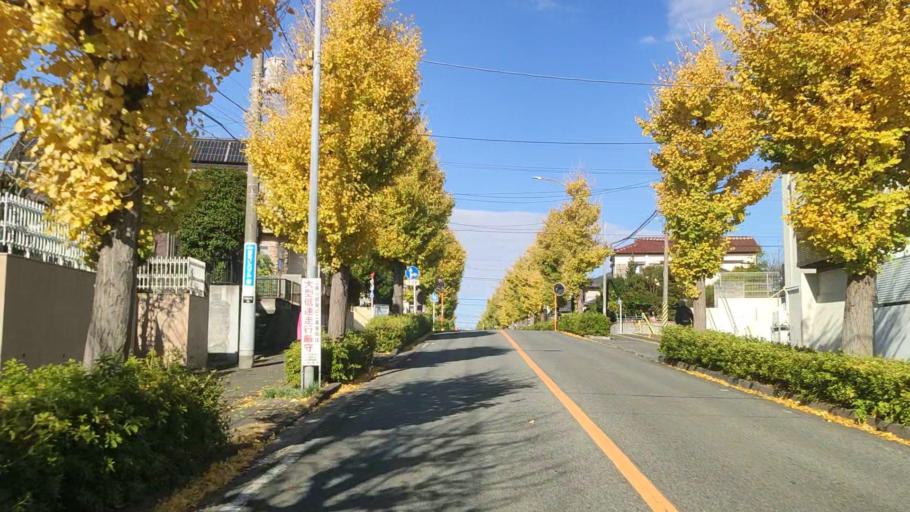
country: JP
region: Kanagawa
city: Minami-rinkan
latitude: 35.4555
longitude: 139.5348
